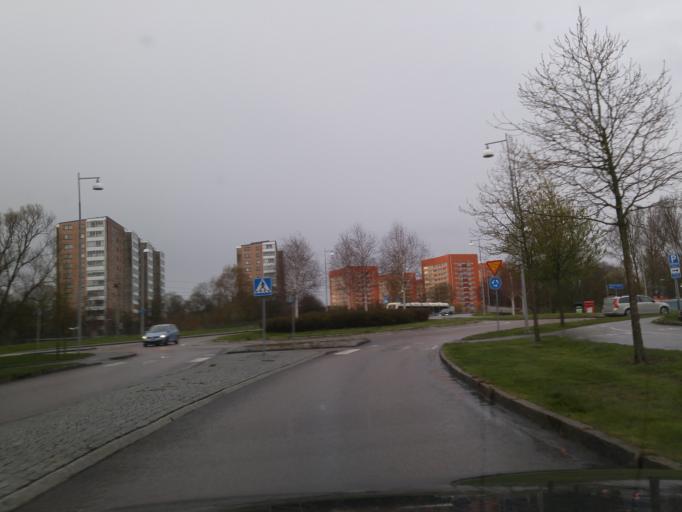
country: SE
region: Vaestra Goetaland
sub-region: Goteborg
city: Majorna
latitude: 57.6540
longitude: 11.9152
